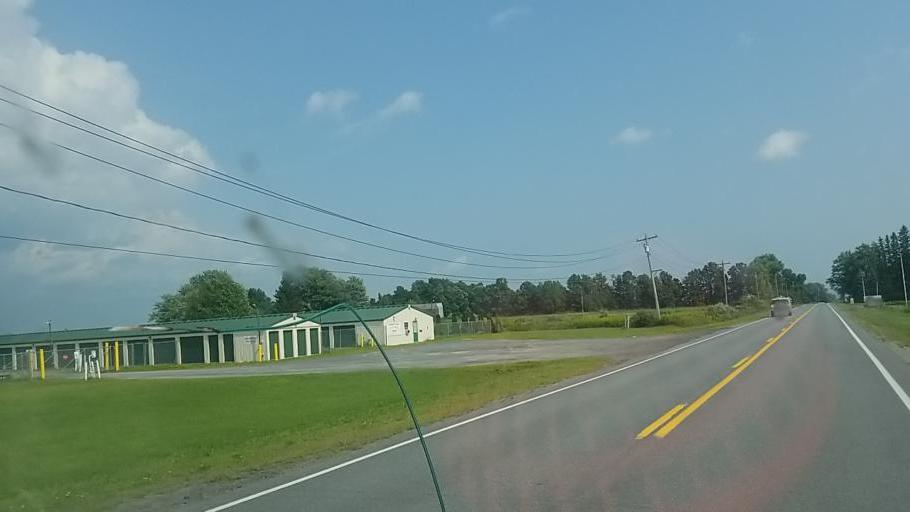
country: US
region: New York
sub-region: Montgomery County
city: Tribes Hill
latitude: 42.9858
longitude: -74.3223
